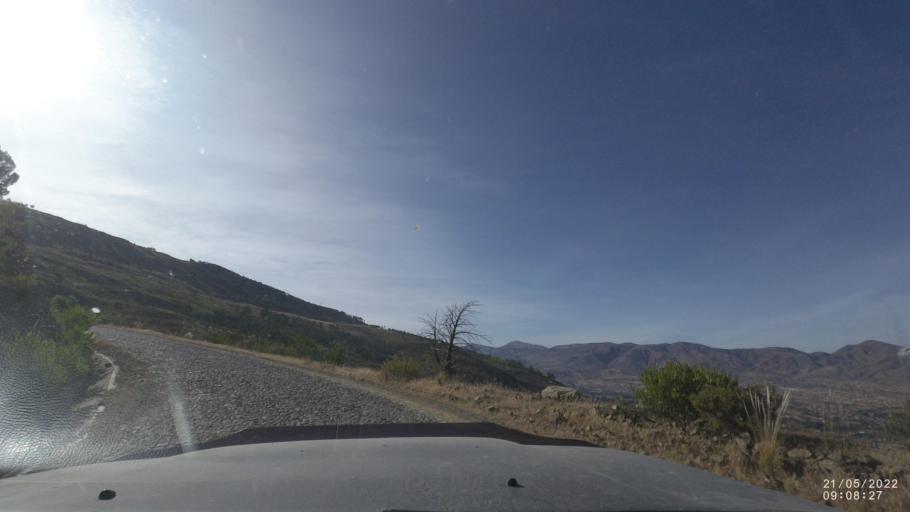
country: BO
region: Cochabamba
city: Cochabamba
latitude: -17.3762
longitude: -66.0235
